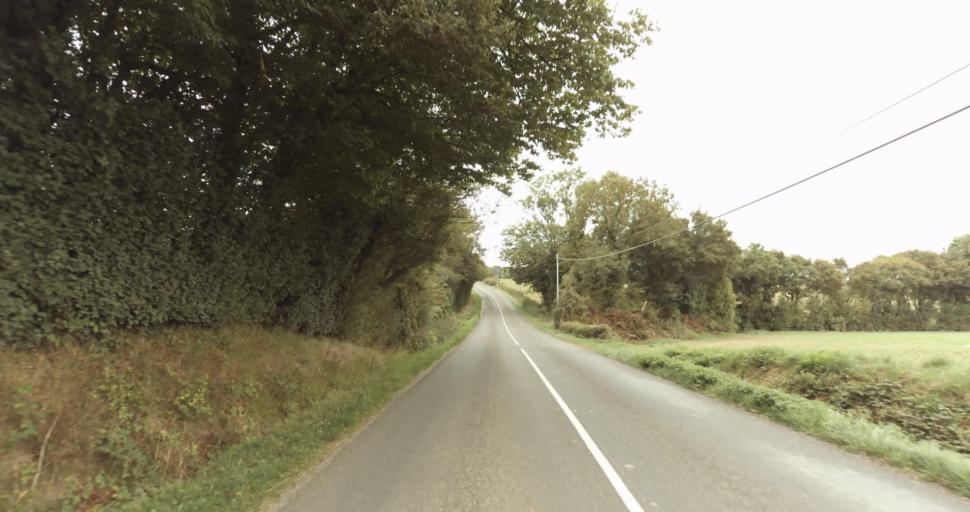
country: FR
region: Lower Normandy
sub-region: Departement de l'Orne
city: Gace
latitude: 48.6940
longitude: 0.2868
